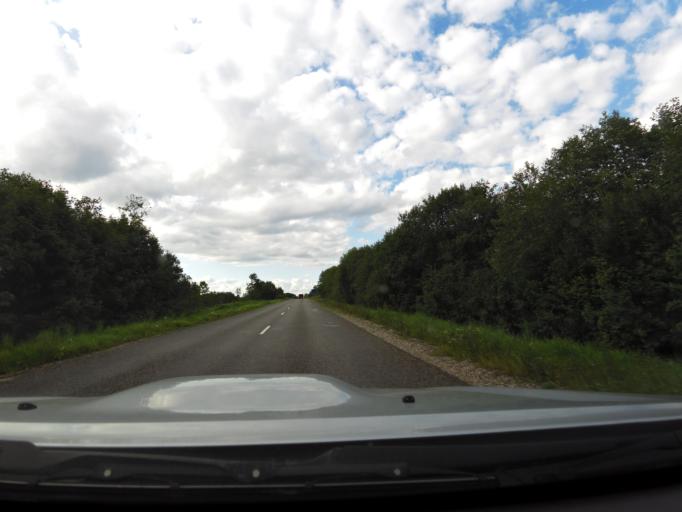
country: LV
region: Akniste
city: Akniste
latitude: 56.0188
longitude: 25.9234
